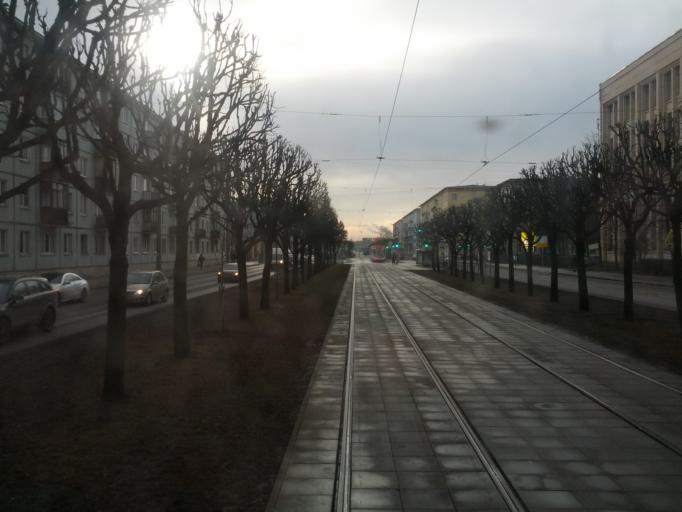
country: RU
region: St.-Petersburg
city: Centralniy
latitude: 59.9234
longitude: 30.4181
